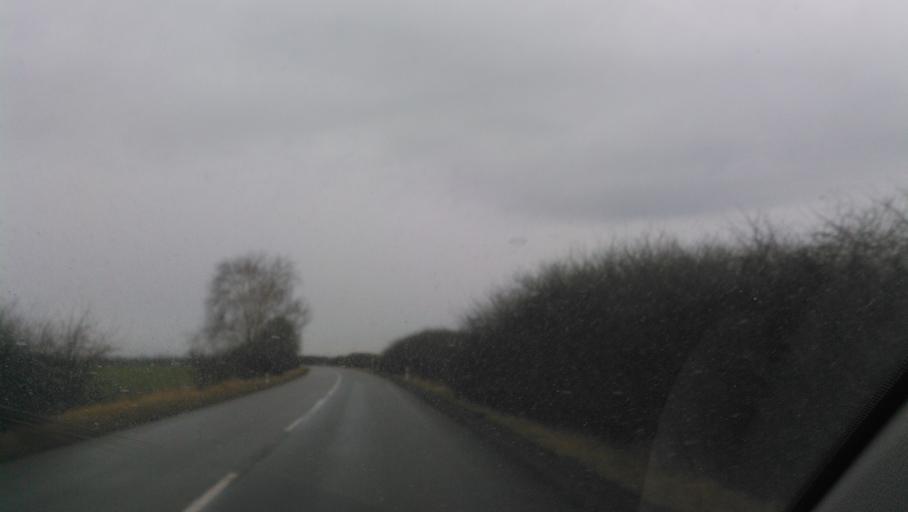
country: SK
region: Nitriansky
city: Sellye
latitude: 48.0919
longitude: 17.9057
